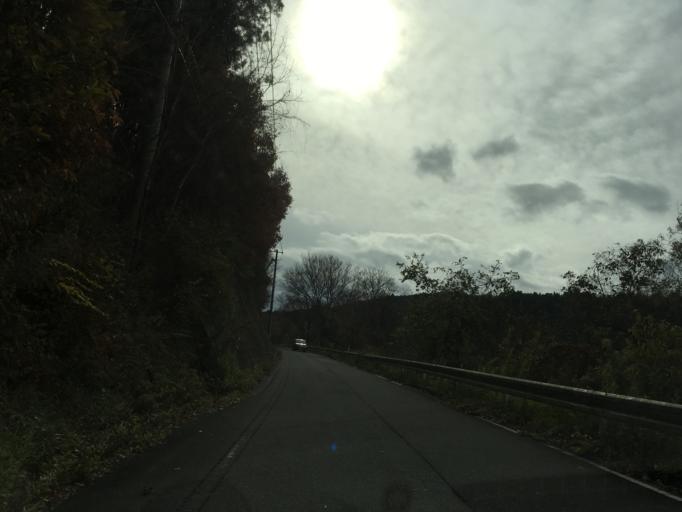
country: JP
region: Iwate
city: Ichinoseki
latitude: 38.7750
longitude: 141.2681
